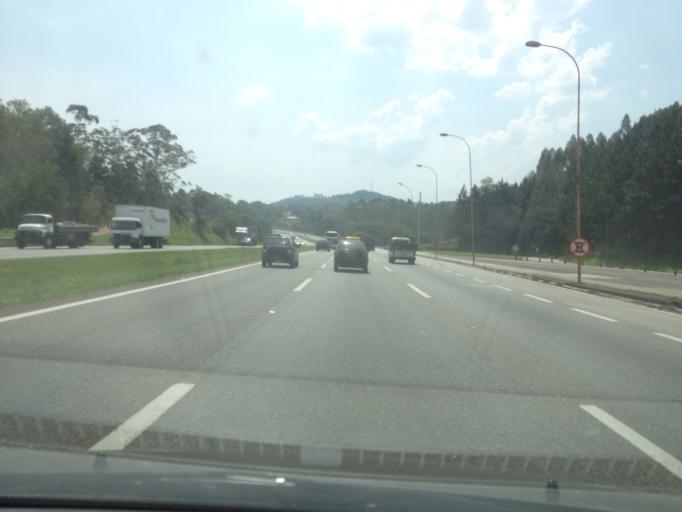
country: BR
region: Sao Paulo
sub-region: Pirapora Do Bom Jesus
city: Pirapora do Bom Jesus
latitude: -23.4753
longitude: -47.0024
